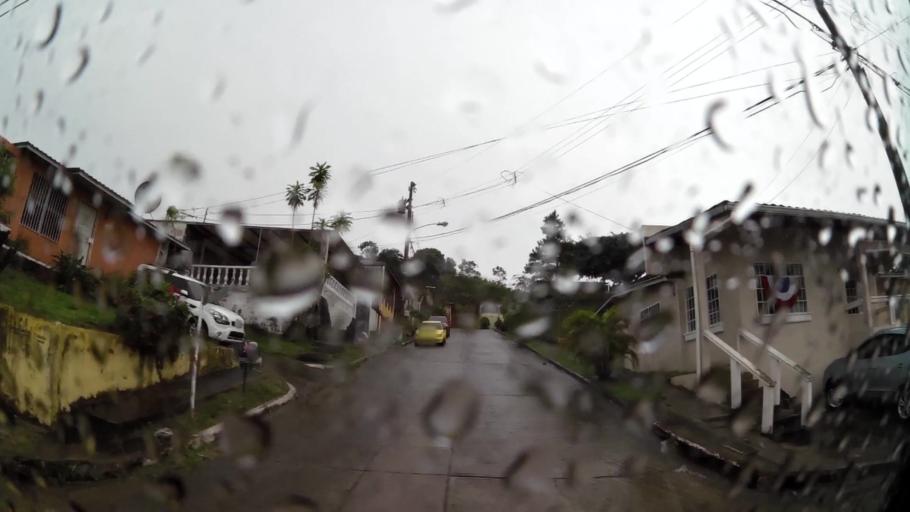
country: PA
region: Panama
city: San Miguelito
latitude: 9.0492
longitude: -79.4730
